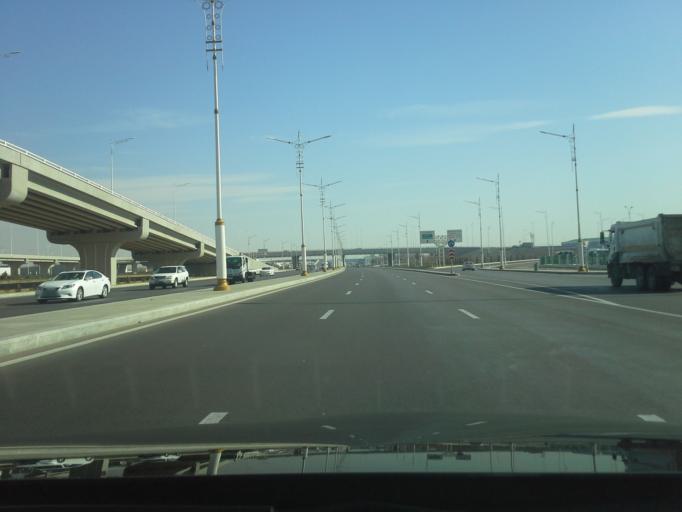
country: TM
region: Ahal
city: Ashgabat
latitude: 37.9287
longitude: 58.4232
